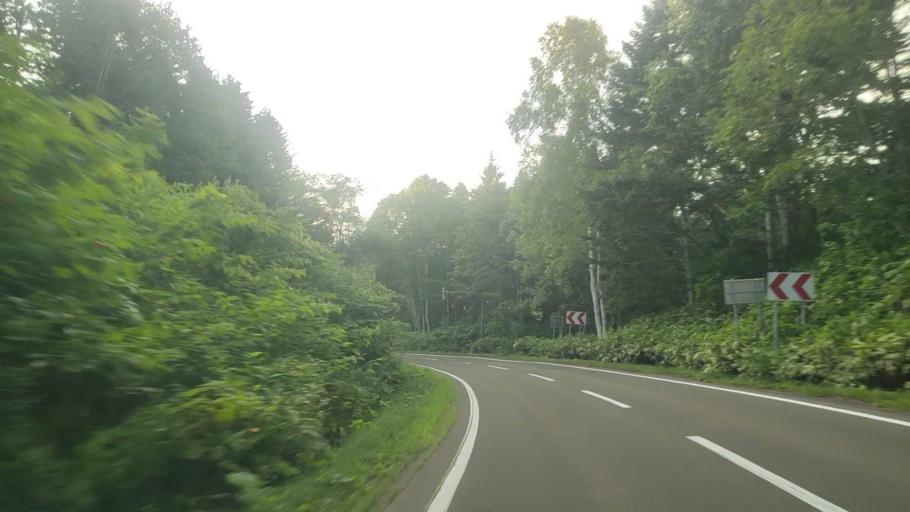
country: JP
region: Hokkaido
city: Bibai
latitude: 43.1437
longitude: 142.0908
